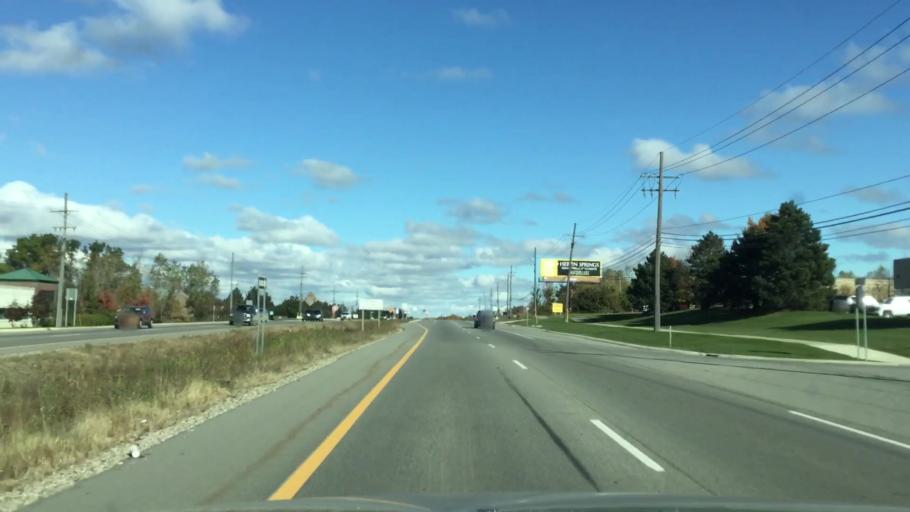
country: US
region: Michigan
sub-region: Oakland County
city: Auburn Hills
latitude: 42.7138
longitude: -83.2425
